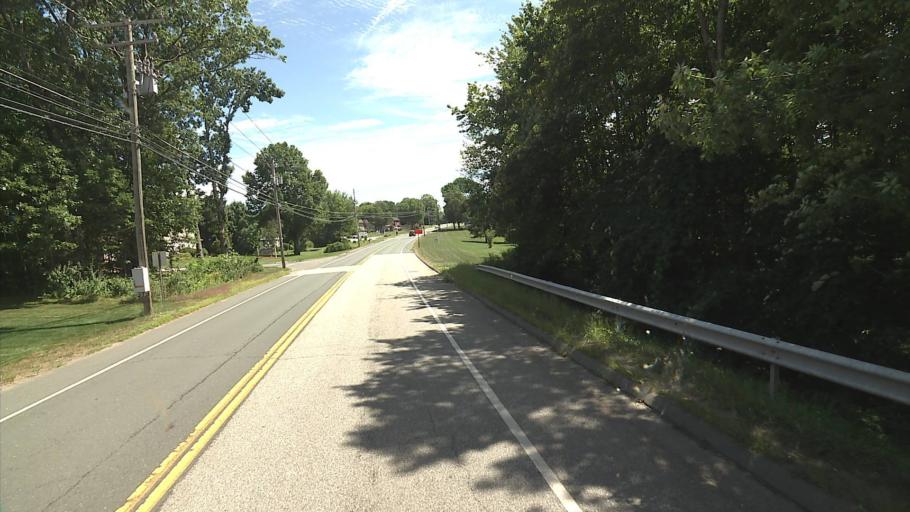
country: US
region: Connecticut
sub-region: Tolland County
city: Tolland
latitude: 41.8547
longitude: -72.3405
